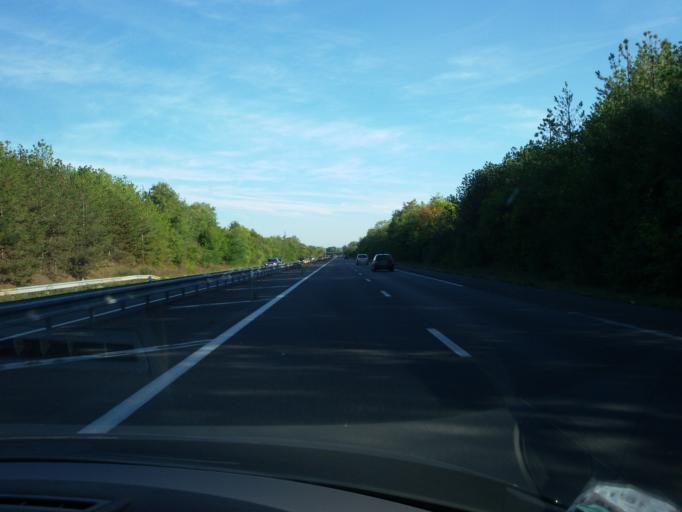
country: FR
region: Centre
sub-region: Departement du Cher
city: Foecy
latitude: 47.1555
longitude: 2.1838
